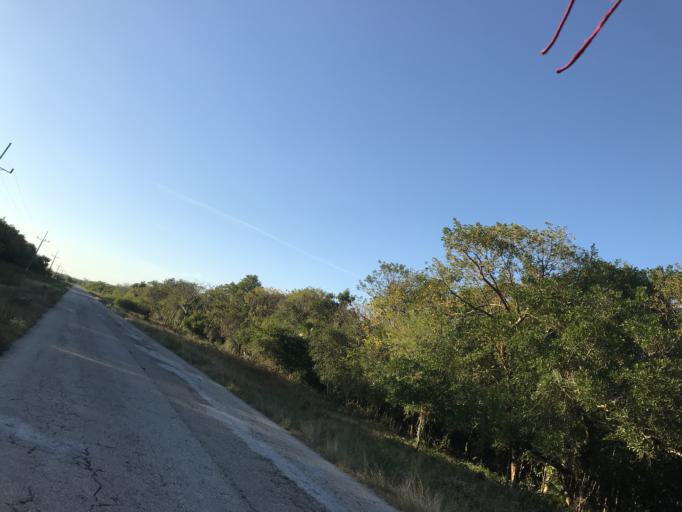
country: CU
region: Cienfuegos
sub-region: Municipio de Aguada de Pasajeros
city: Aguada de Pasajeros
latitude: 22.0779
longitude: -81.0666
